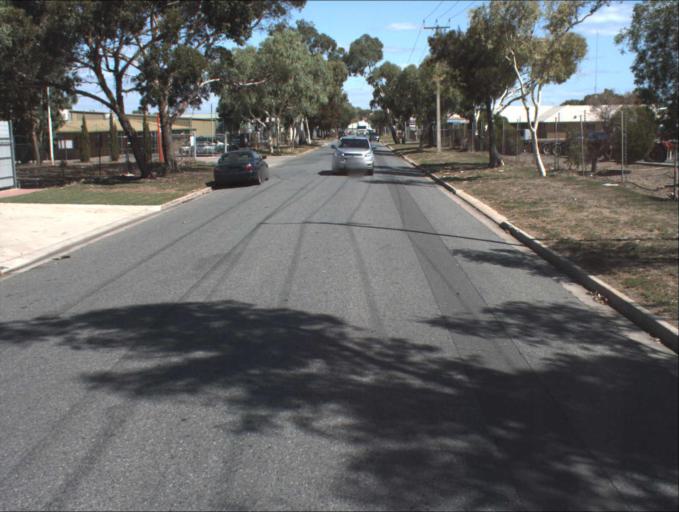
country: AU
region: South Australia
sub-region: Charles Sturt
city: Woodville North
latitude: -34.8419
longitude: 138.5550
